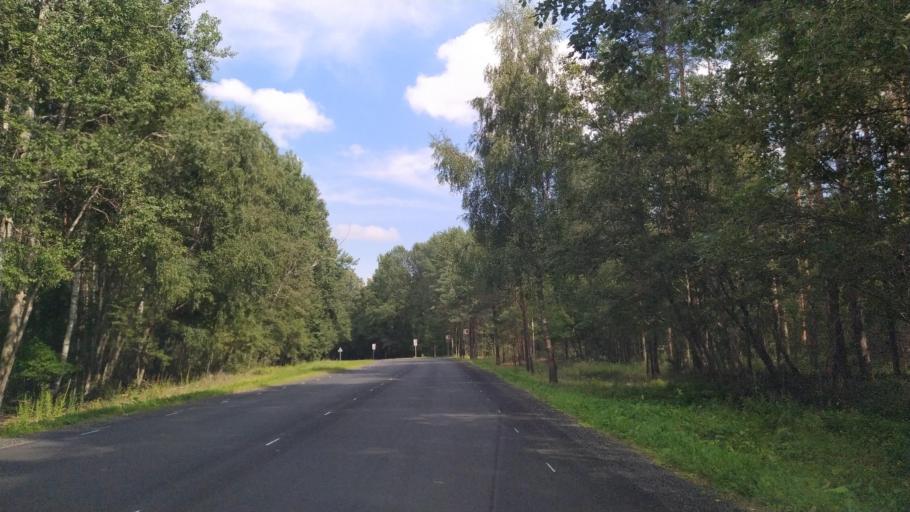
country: RU
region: Pskov
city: Porkhov
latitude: 57.7355
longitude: 29.4106
